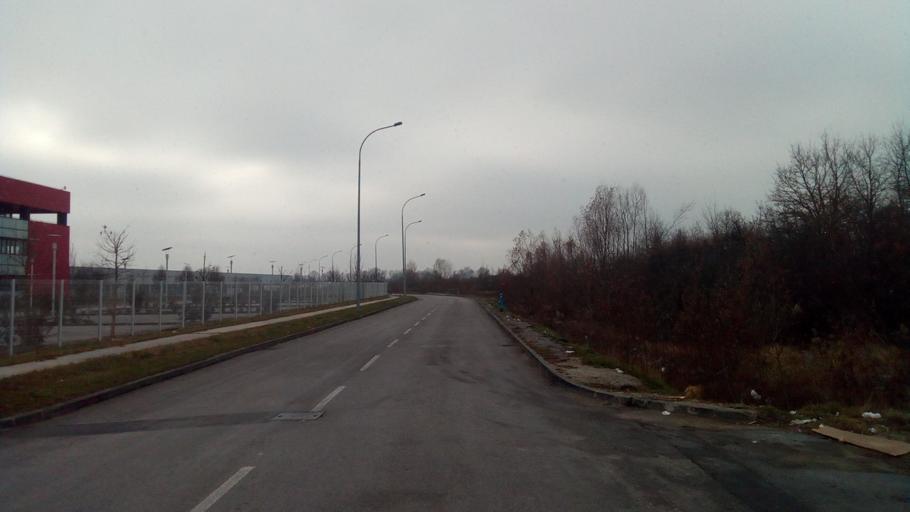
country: HR
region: Zagrebacka
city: Jastrebarsko
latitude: 45.6515
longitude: 15.6776
